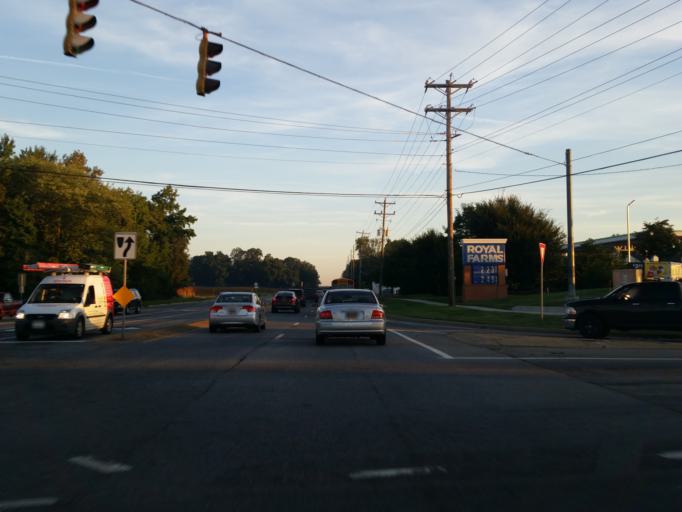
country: US
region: Delaware
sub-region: New Castle County
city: Brookside
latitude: 39.6422
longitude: -75.7300
